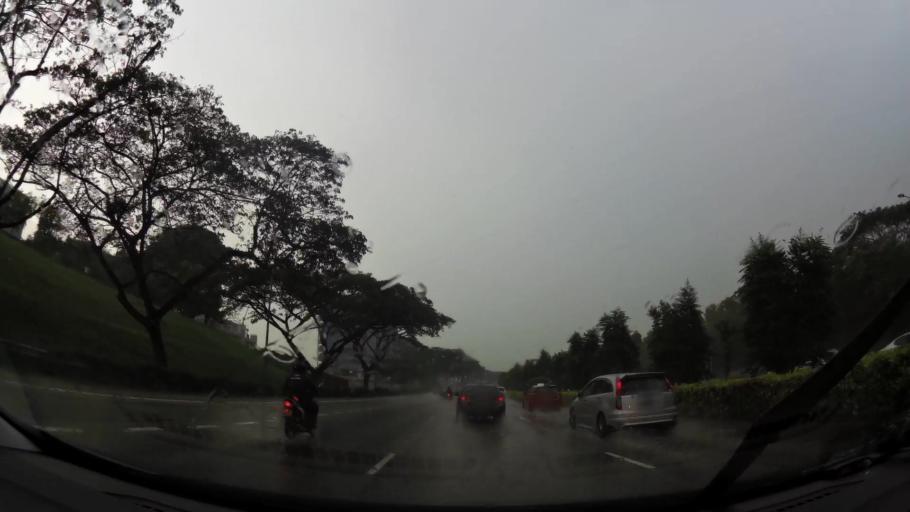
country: MY
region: Johor
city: Kampung Pasir Gudang Baru
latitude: 1.3787
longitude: 103.9227
